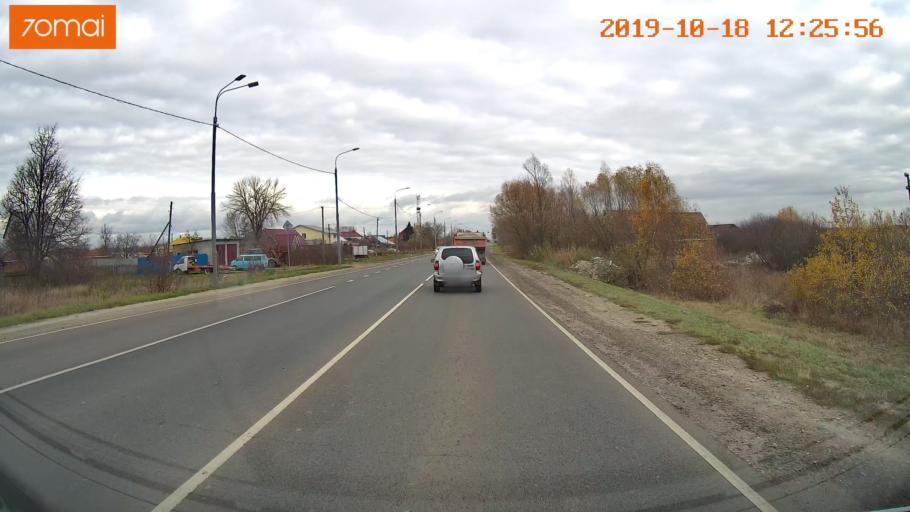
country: RU
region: Rjazan
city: Rybnoye
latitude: 54.5541
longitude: 39.5265
